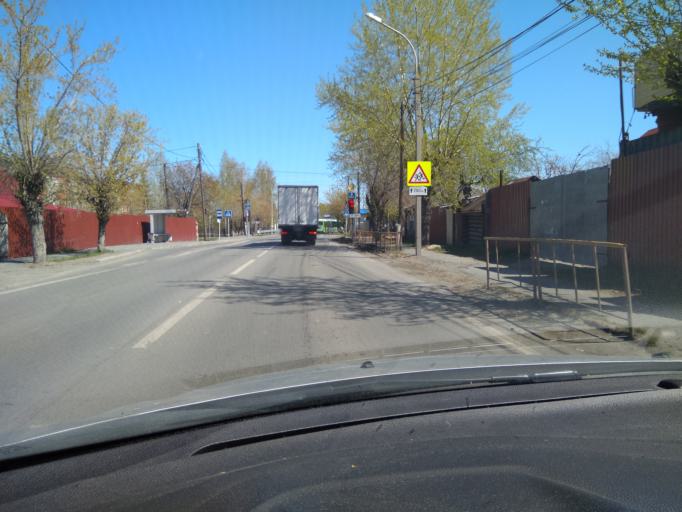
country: RU
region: Tjumen
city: Moskovskiy
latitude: 57.1572
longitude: 65.4511
